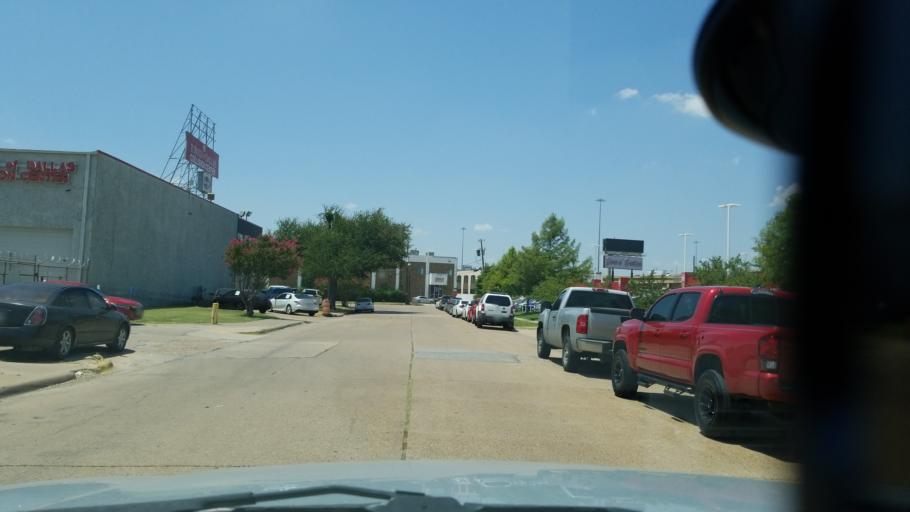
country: US
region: Texas
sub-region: Dallas County
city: Farmers Branch
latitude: 32.9073
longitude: -96.8892
